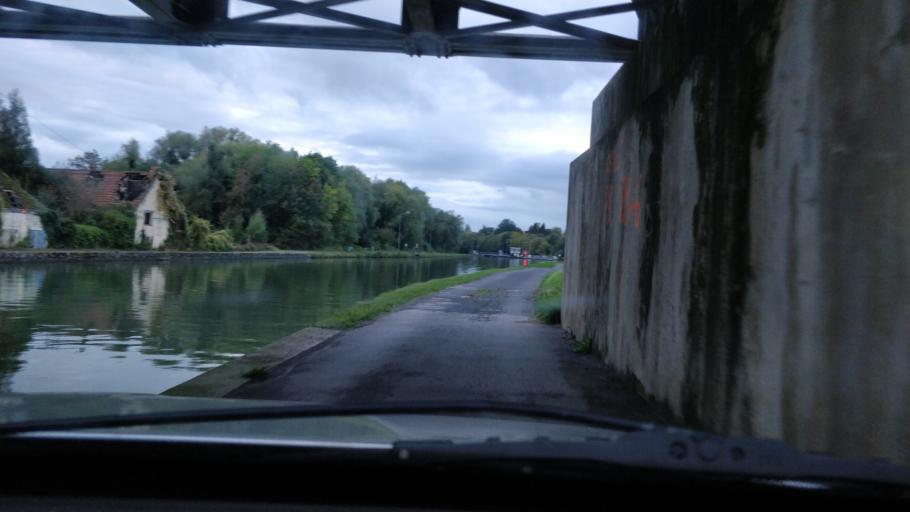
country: FR
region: Picardie
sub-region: Departement de l'Oise
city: Cambronne-les-Ribecourt
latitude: 49.5006
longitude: 2.9143
